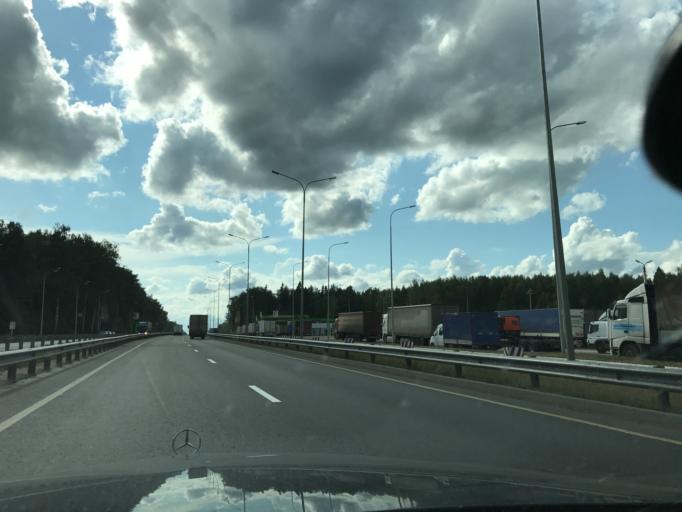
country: RU
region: Vladimir
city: Lakinsk
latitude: 55.9961
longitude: 39.8931
